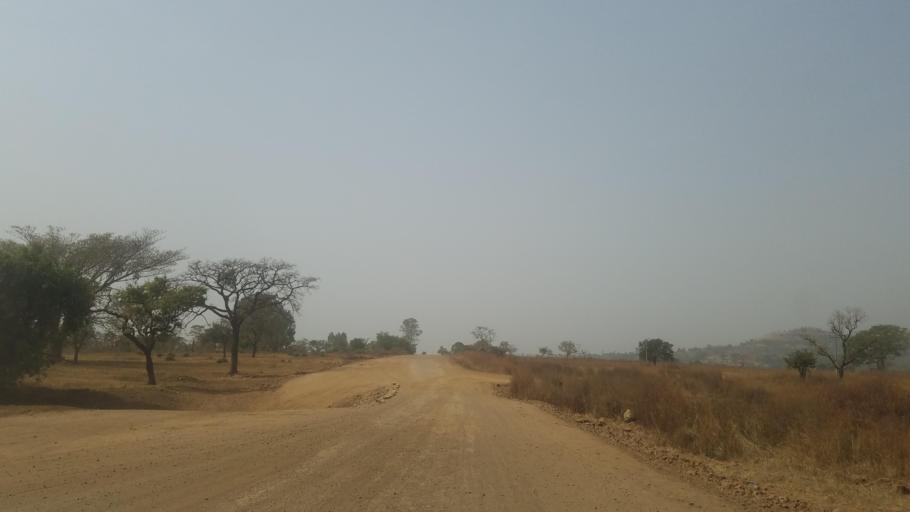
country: ET
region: Amhara
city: Bure
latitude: 10.9342
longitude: 36.4690
